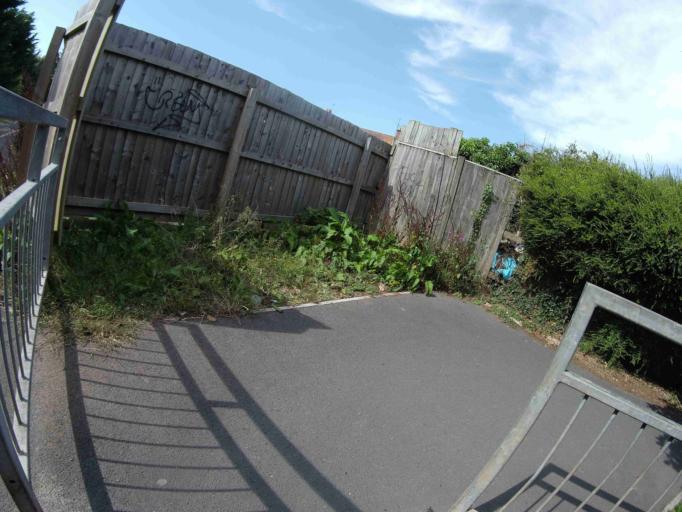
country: GB
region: England
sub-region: Devon
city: Exmouth
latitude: 50.6239
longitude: -3.3886
